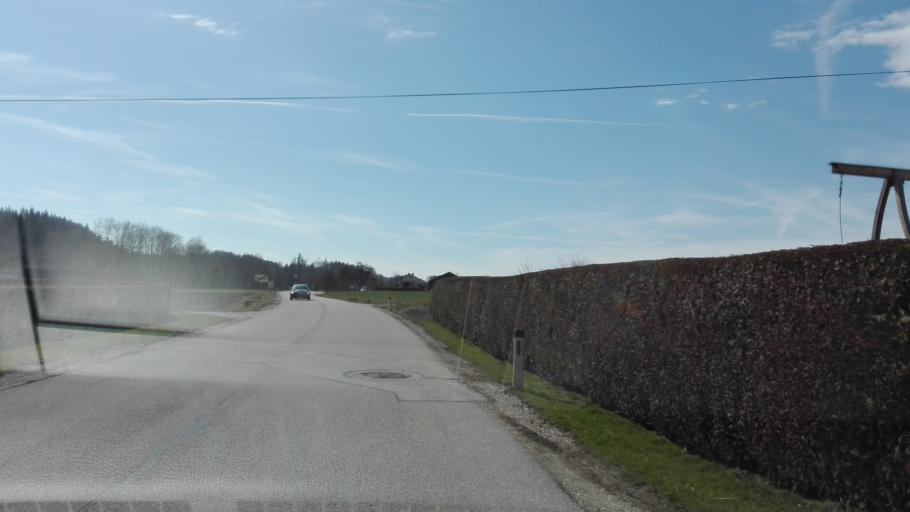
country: AT
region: Upper Austria
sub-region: Politischer Bezirk Grieskirchen
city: Grieskirchen
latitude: 48.2200
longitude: 13.7979
